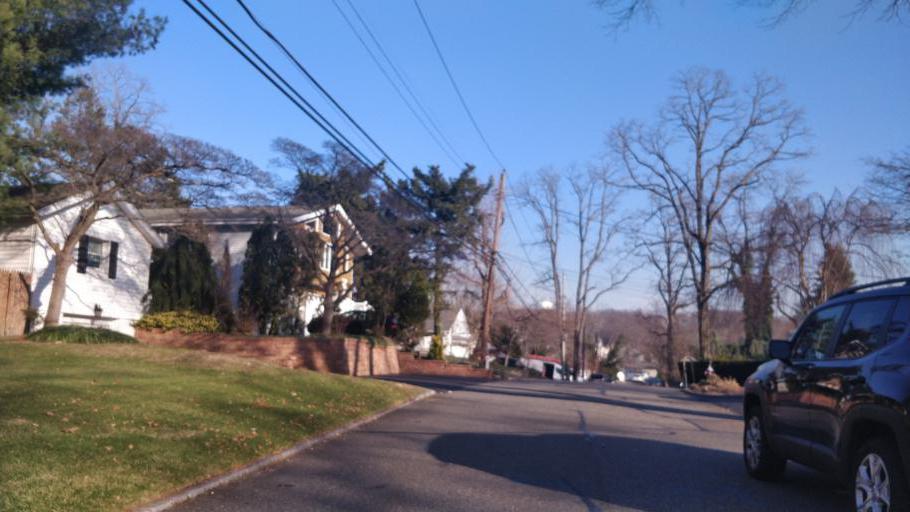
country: US
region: New York
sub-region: Nassau County
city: Bayville
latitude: 40.9055
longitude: -73.5752
